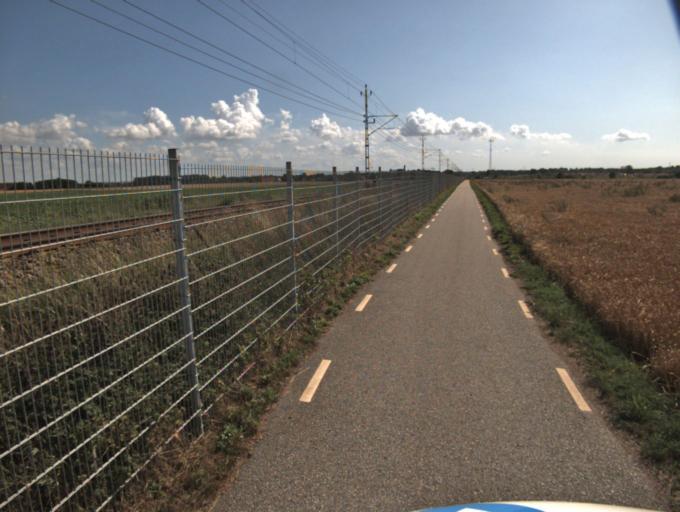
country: SE
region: Skane
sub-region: Kavlinge Kommun
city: Kaevlinge
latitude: 55.8134
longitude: 13.1093
